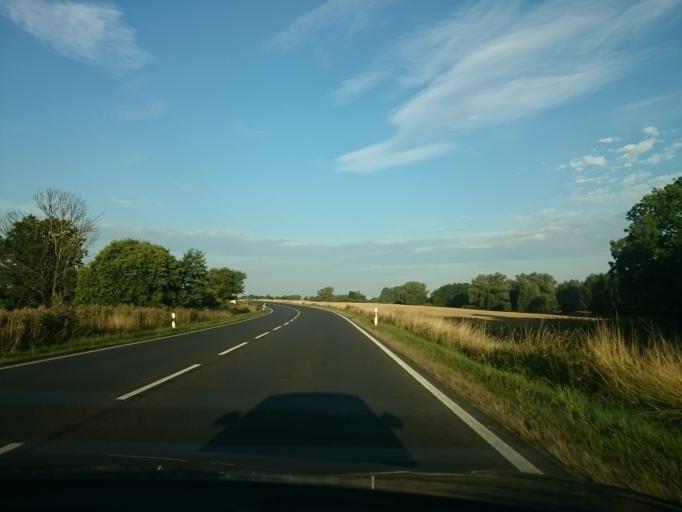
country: DE
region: Mecklenburg-Vorpommern
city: Karlshagen
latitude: 54.0621
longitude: 13.8224
